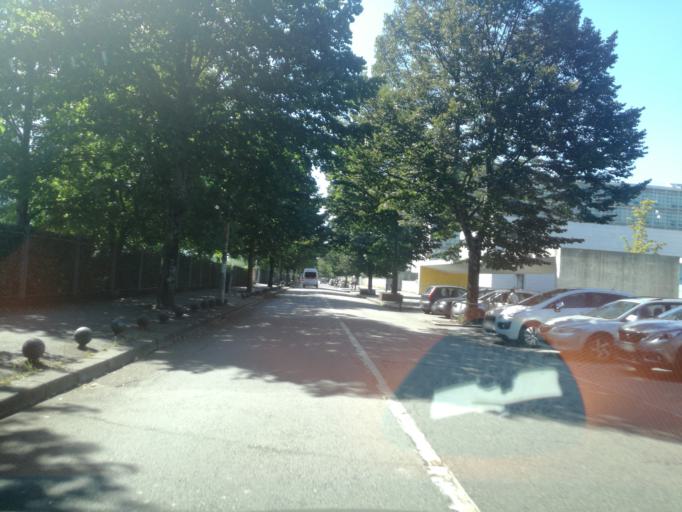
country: PT
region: Porto
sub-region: Matosinhos
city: Sao Mamede de Infesta
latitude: 41.1785
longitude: -8.5992
